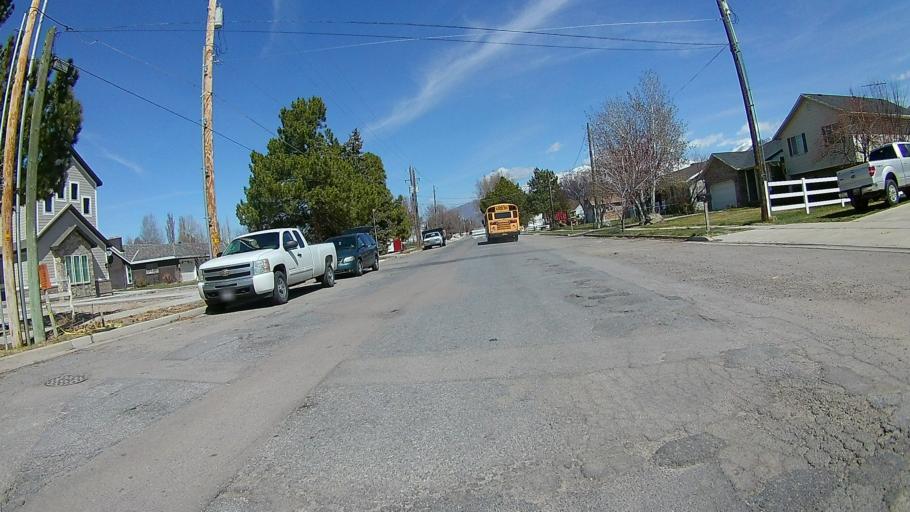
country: US
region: Utah
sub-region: Utah County
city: American Fork
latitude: 40.3652
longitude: -111.8014
